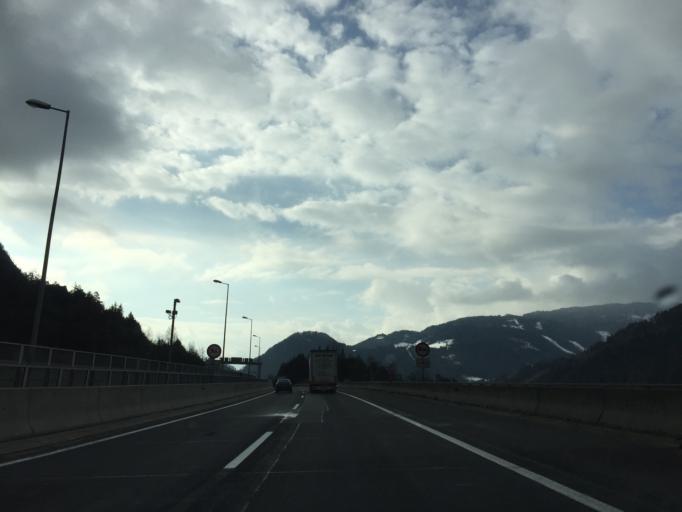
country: AT
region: Salzburg
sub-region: Politischer Bezirk Sankt Johann im Pongau
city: Werfen
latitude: 47.5167
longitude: 13.1695
